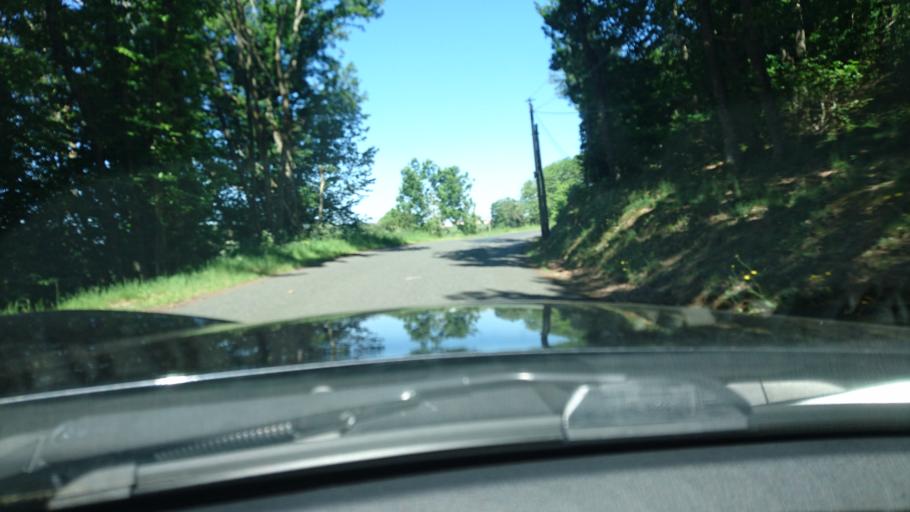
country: FR
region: Rhone-Alpes
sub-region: Departement de la Loire
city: Violay
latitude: 45.8411
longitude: 4.3692
